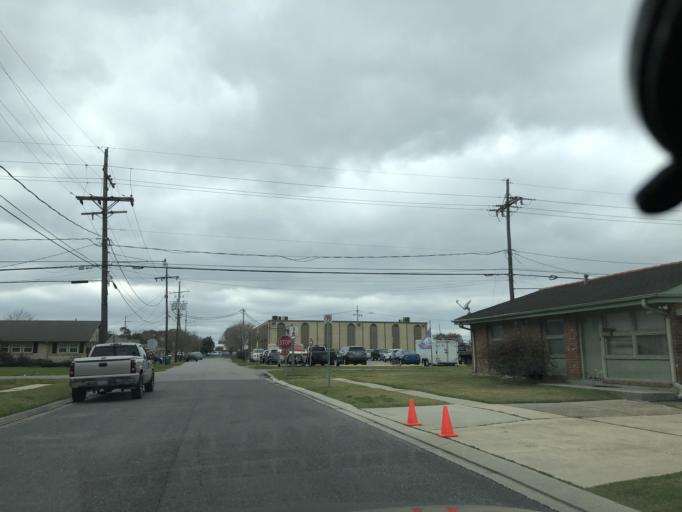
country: US
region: Louisiana
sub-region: Jefferson Parish
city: Metairie
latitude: 29.9915
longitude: -90.1537
